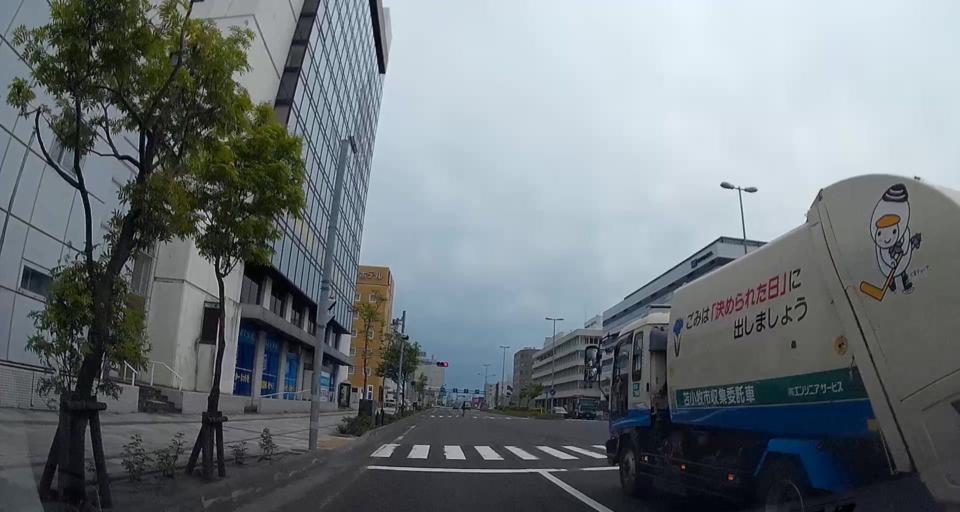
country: JP
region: Hokkaido
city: Tomakomai
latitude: 42.6336
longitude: 141.6028
